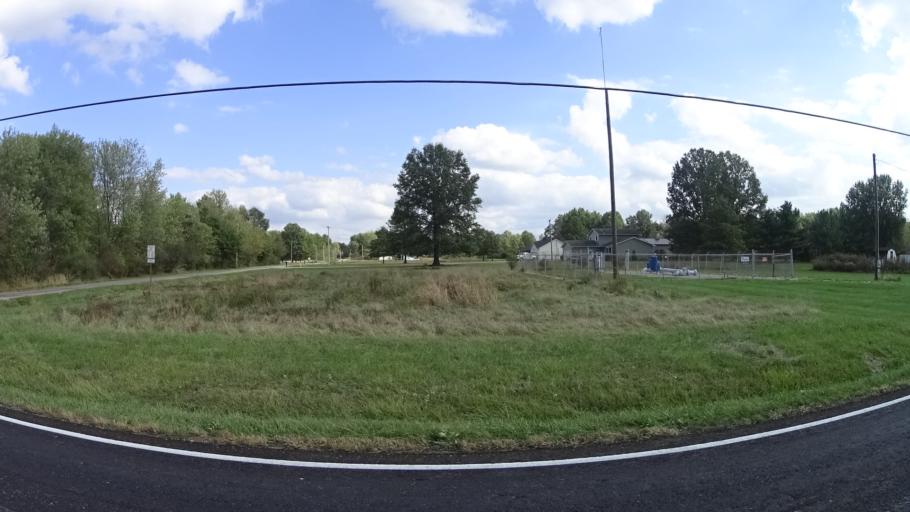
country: US
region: Ohio
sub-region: Lorain County
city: Grafton
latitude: 41.2641
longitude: -82.0804
